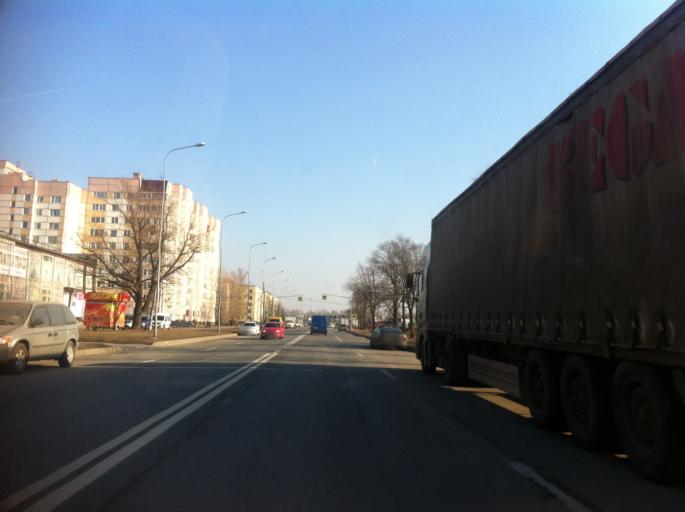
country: RU
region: St.-Petersburg
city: Dachnoye
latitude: 59.8347
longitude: 30.2475
